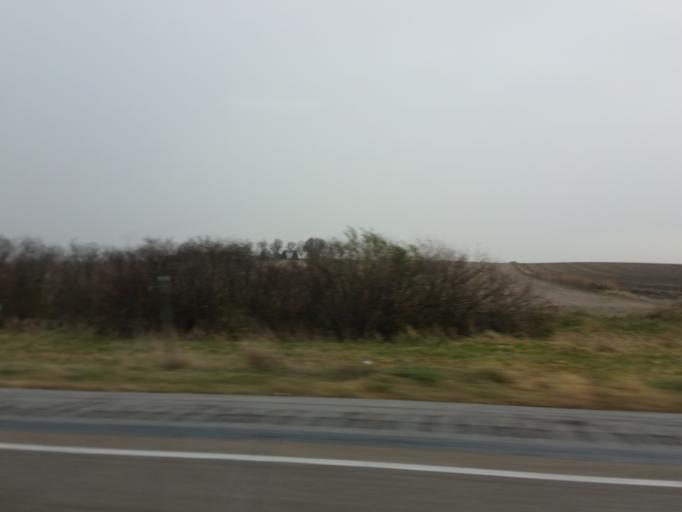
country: US
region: Iowa
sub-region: Cedar County
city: Durant
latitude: 41.6331
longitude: -90.8895
